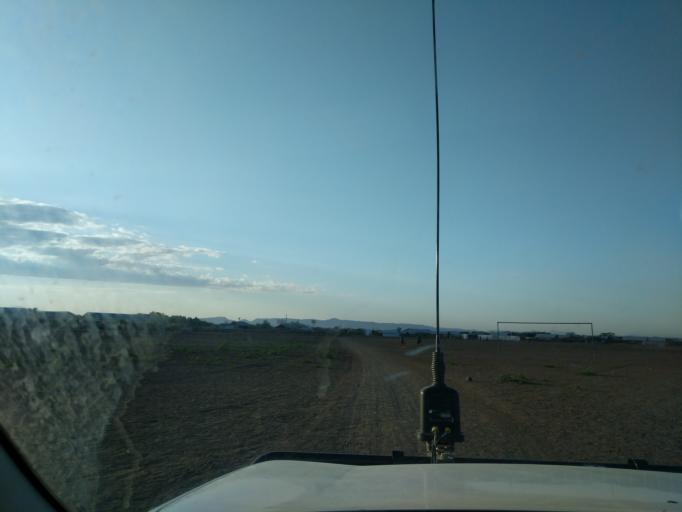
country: UG
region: Northern Region
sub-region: Kaabong District
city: Kaabong
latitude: 3.7583
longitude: 34.8092
